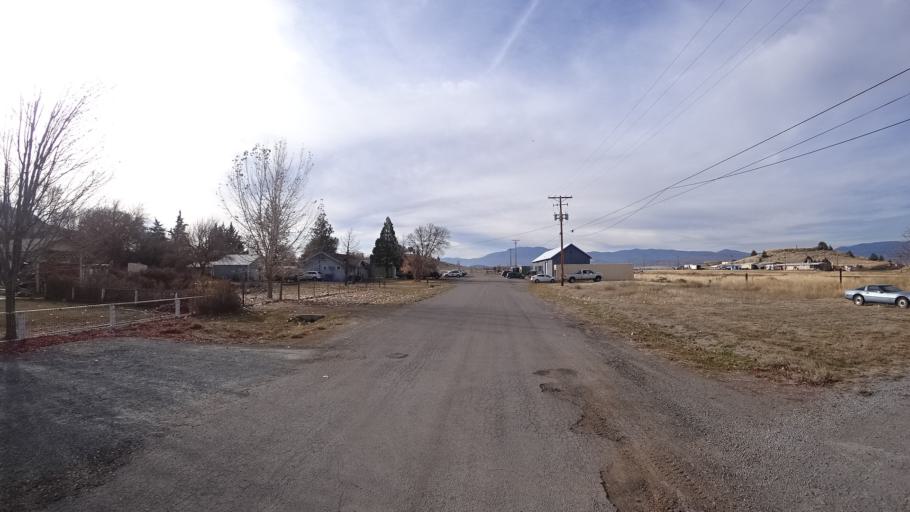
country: US
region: California
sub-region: Siskiyou County
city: Montague
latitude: 41.7250
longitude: -122.5277
